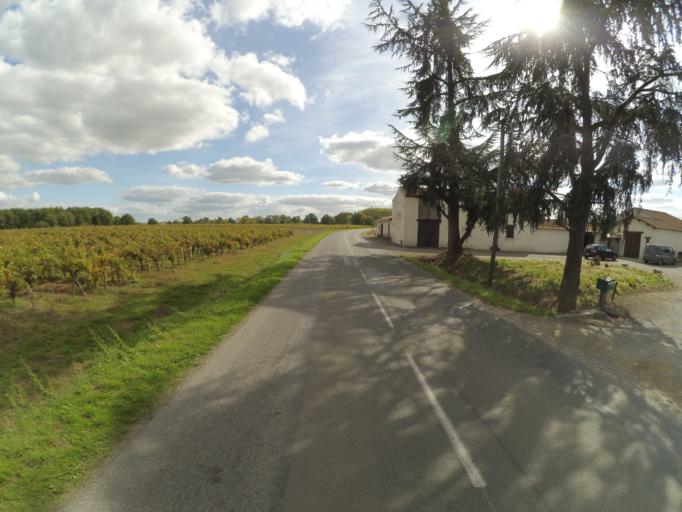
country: FR
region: Pays de la Loire
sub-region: Departement de la Loire-Atlantique
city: Le Loroux-Bottereau
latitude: 47.2068
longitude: -1.3486
